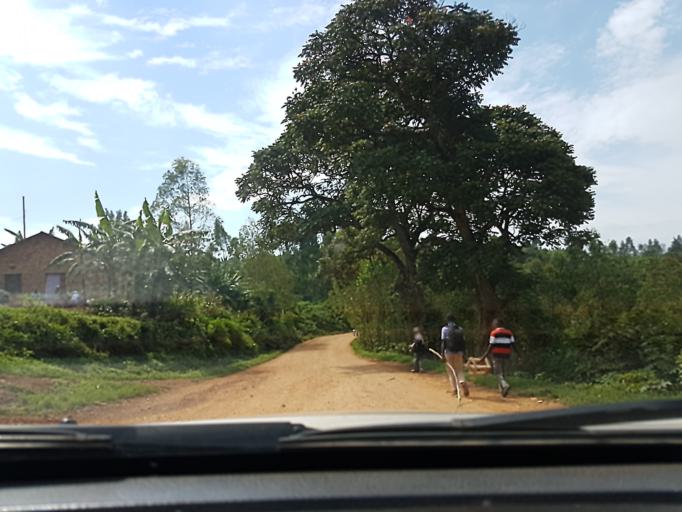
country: CD
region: South Kivu
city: Bukavu
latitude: -2.6221
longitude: 28.8772
